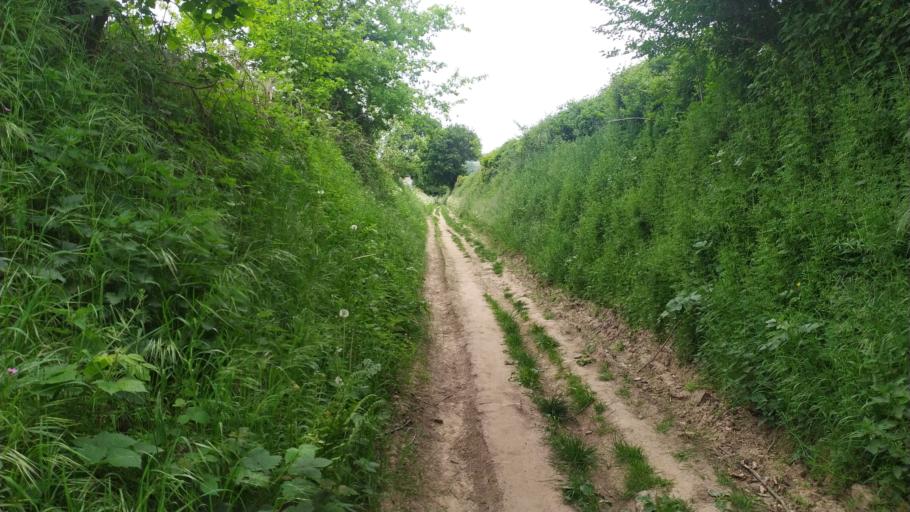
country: BE
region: Flanders
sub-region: Provincie Vlaams-Brabant
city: Huldenberg
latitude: 50.8361
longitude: 4.5873
